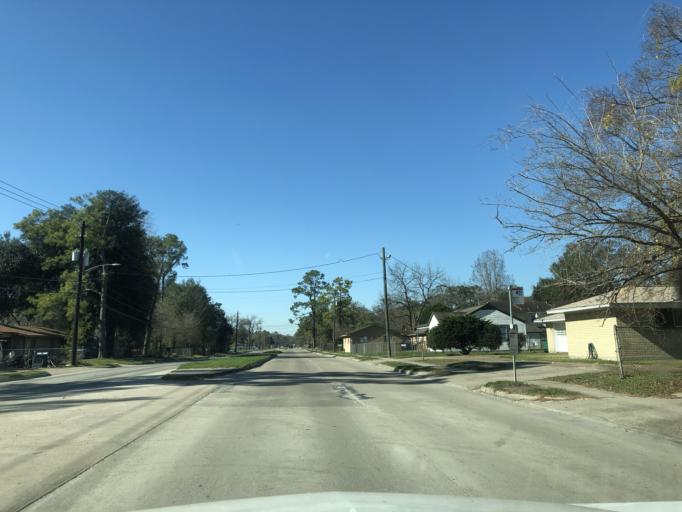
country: US
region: Texas
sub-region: Harris County
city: Jacinto City
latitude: 29.8314
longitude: -95.2957
